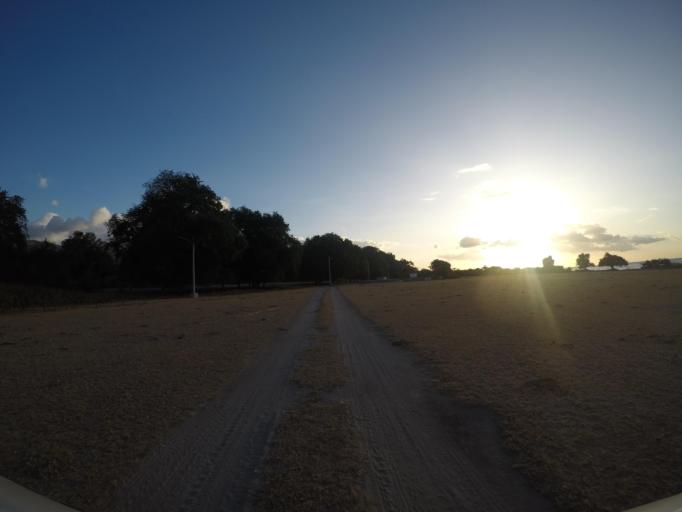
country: TL
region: Lautem
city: Lospalos
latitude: -8.3245
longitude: 126.9938
